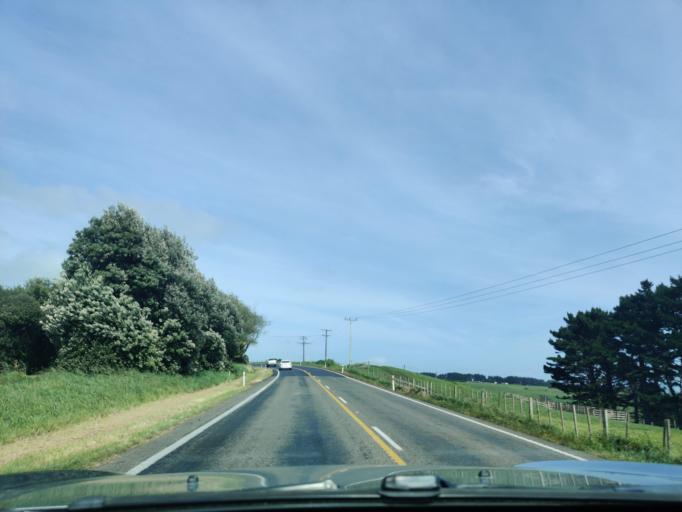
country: NZ
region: Taranaki
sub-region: South Taranaki District
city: Hawera
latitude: -39.6492
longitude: 174.3847
